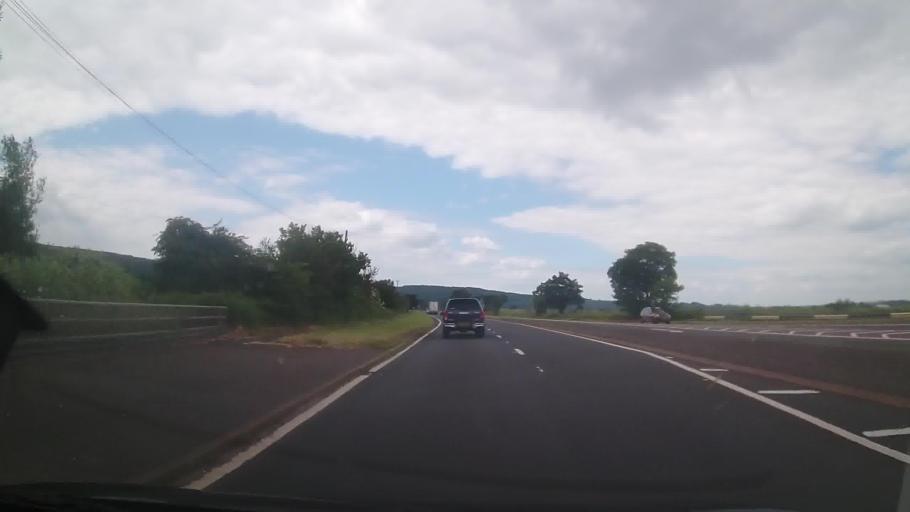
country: GB
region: England
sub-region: Herefordshire
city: Wellington
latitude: 52.1294
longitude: -2.7313
